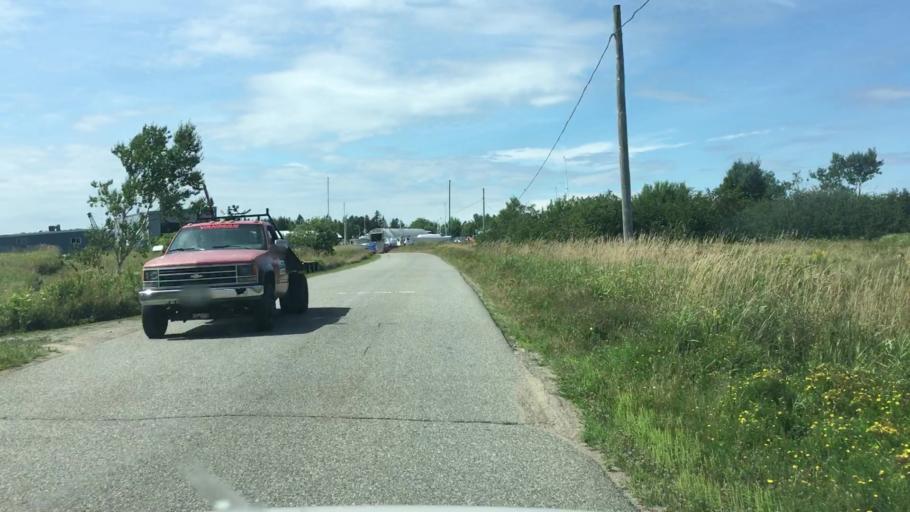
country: US
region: Maine
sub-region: Washington County
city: Eastport
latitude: 44.9068
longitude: -67.0093
